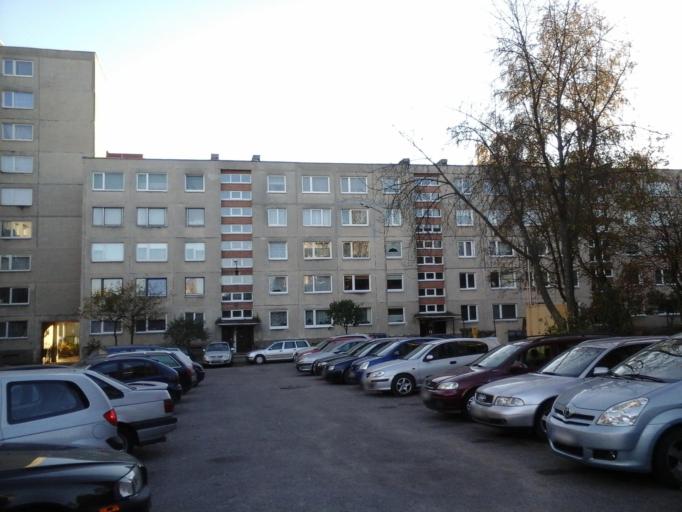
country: LT
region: Vilnius County
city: Justiniskes
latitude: 54.6941
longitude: 25.2114
